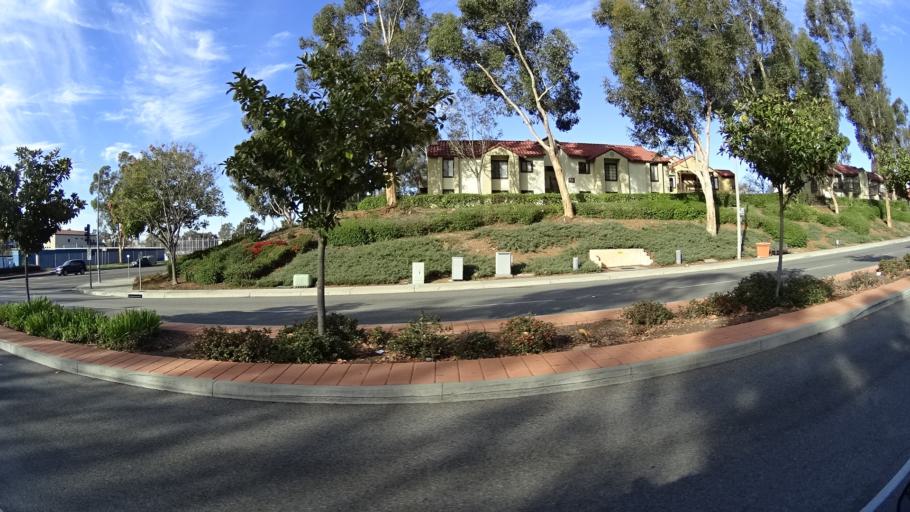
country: US
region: California
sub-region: Orange County
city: Trabuco Canyon
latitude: 33.6447
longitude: -117.5779
